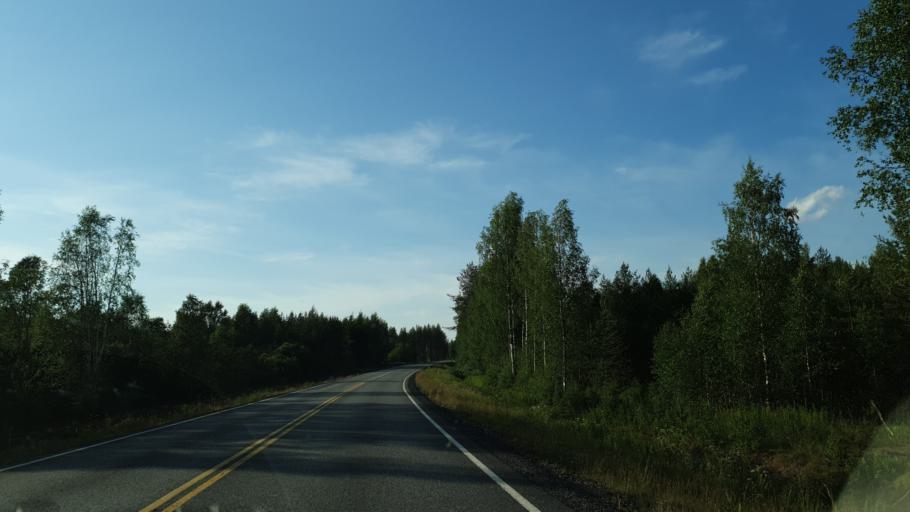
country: FI
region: Kainuu
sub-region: Kehys-Kainuu
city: Kuhmo
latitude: 64.0783
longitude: 29.4875
